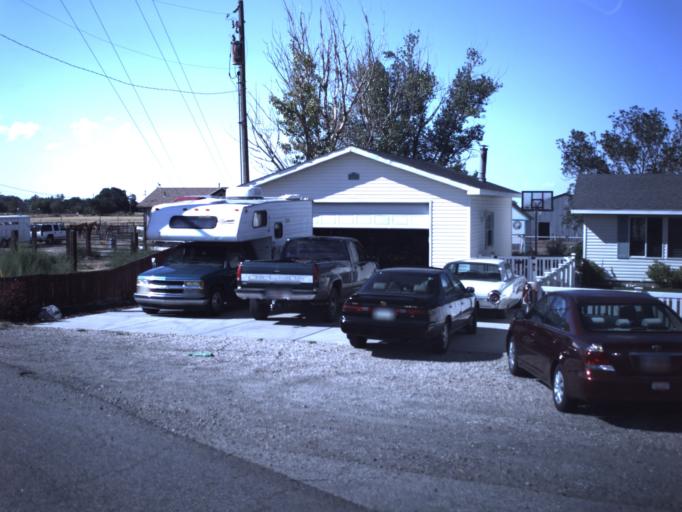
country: US
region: Utah
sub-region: Tooele County
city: Grantsville
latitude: 40.5922
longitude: -112.4228
